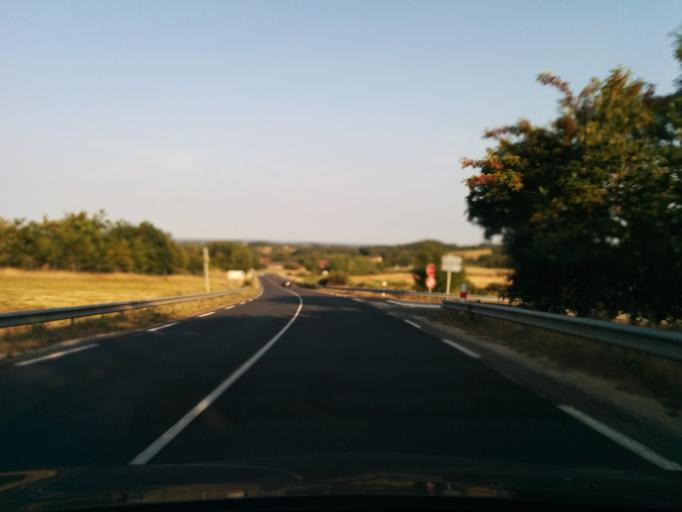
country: FR
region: Midi-Pyrenees
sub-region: Departement du Lot
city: Le Vigan
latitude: 44.6126
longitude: 1.4980
